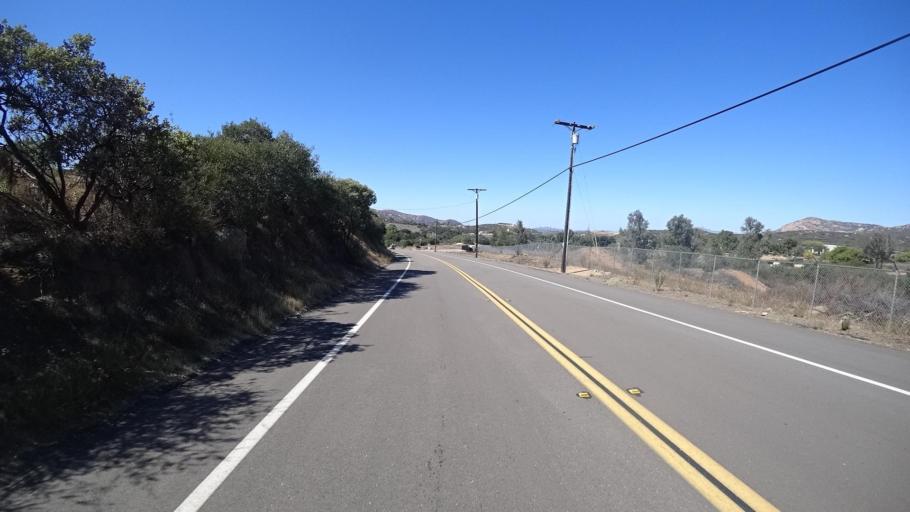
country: US
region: California
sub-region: San Diego County
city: Descanso
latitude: 32.7646
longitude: -116.6790
